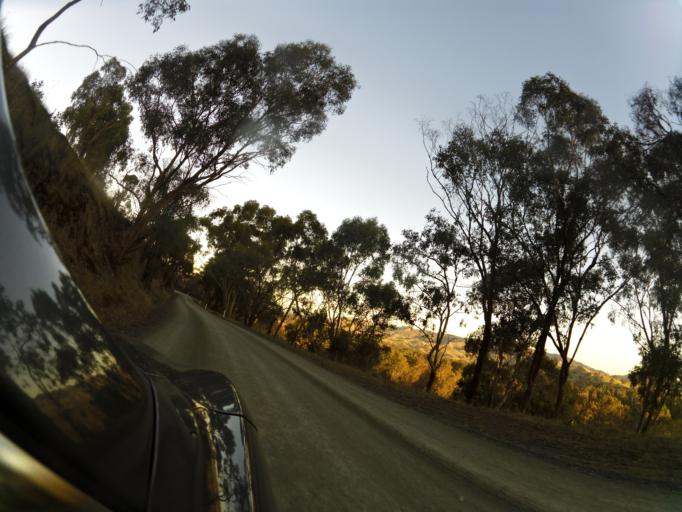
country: AU
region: Victoria
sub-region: Murrindindi
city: Alexandra
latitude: -37.1528
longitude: 145.5261
